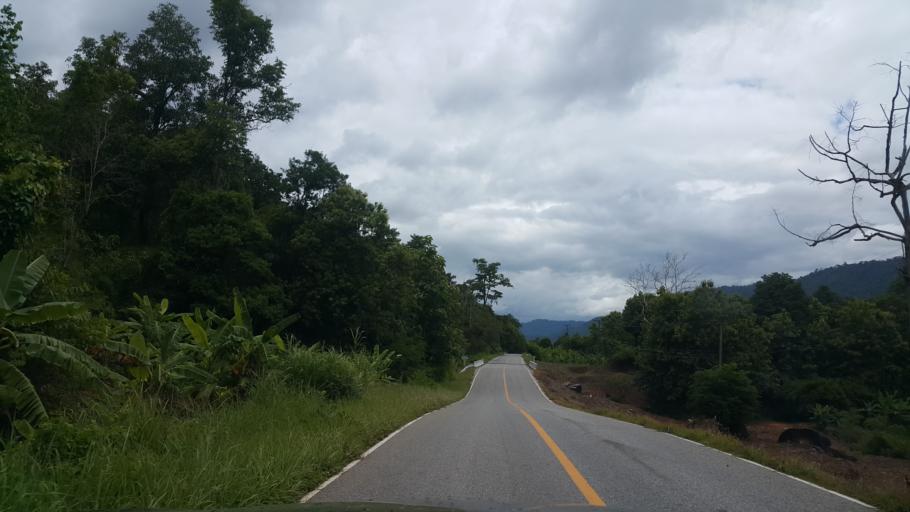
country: TH
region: Phitsanulok
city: Chat Trakan
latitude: 17.3400
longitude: 100.7112
